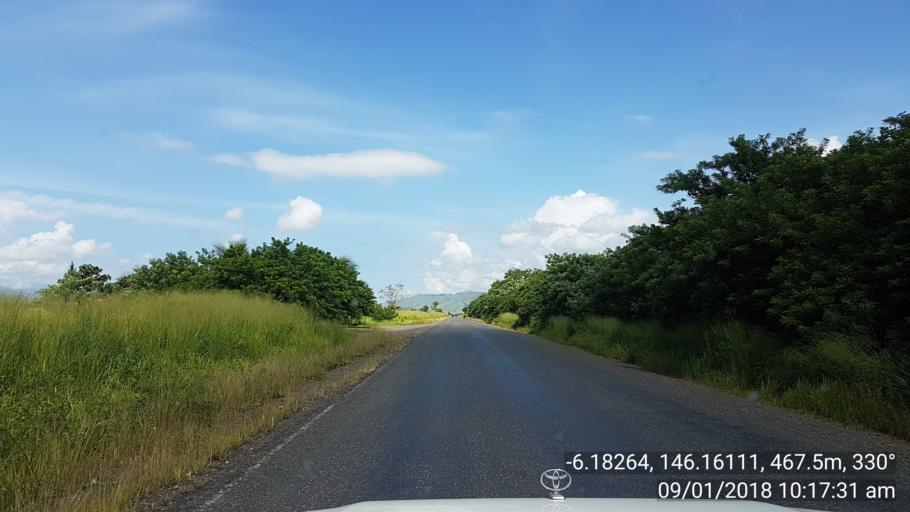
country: PG
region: Eastern Highlands
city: Kainantu
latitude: -6.1826
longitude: 146.1610
